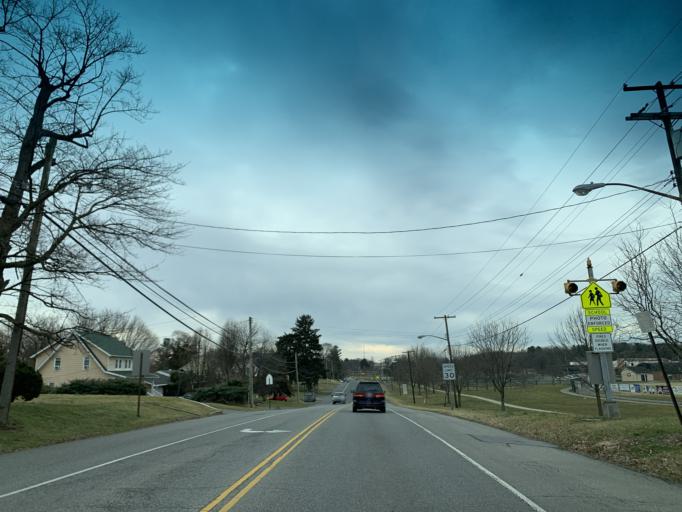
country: US
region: Maryland
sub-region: Washington County
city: Hagerstown
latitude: 39.6233
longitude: -77.7284
